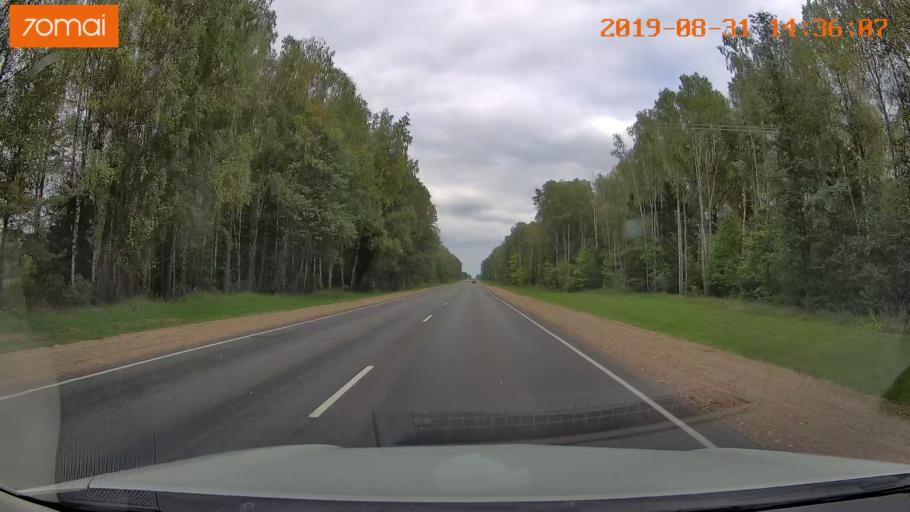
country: RU
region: Smolensk
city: Yekimovichi
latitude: 54.1677
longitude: 33.4720
